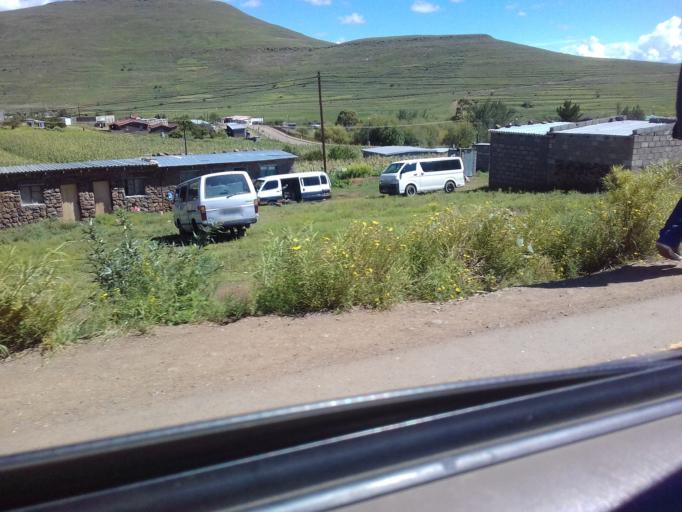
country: LS
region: Thaba-Tseka
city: Thaba-Tseka
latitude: -29.5142
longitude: 28.5974
